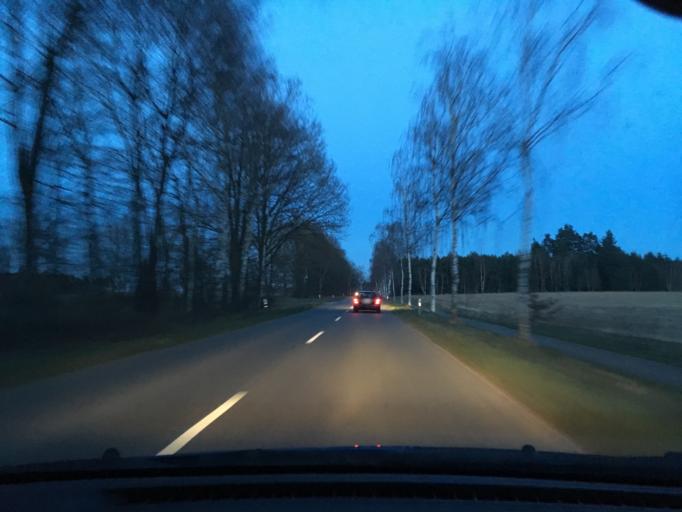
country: DE
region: Lower Saxony
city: Oldendorf
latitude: 53.1774
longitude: 10.2217
